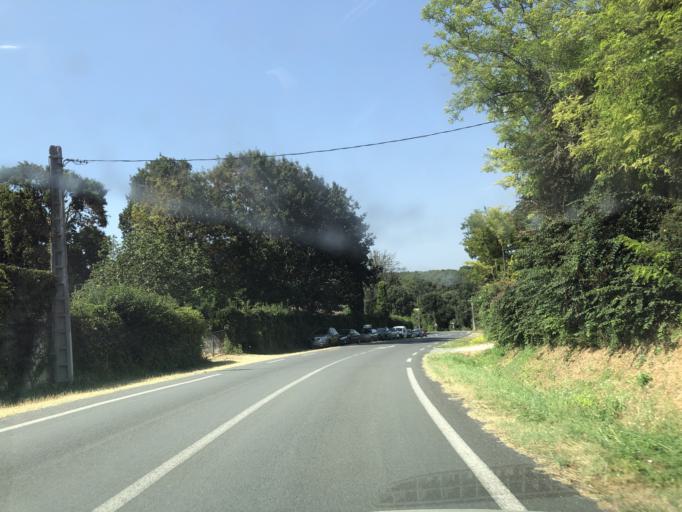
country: FR
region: Poitou-Charentes
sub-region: Departement de la Charente-Maritime
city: Meschers-sur-Gironde
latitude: 45.5635
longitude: -0.9694
